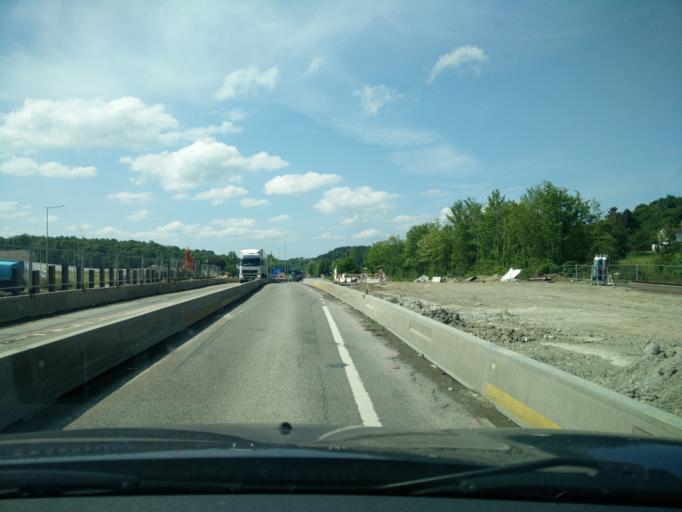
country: BE
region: Wallonia
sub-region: Province de Namur
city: Couvin
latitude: 50.0723
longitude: 4.5080
